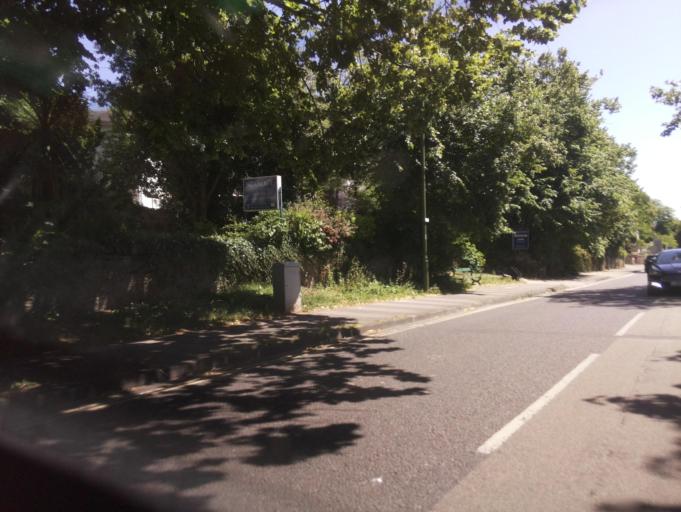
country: GB
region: England
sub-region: Borough of Torbay
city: Torquay
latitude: 50.4669
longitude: -3.5432
